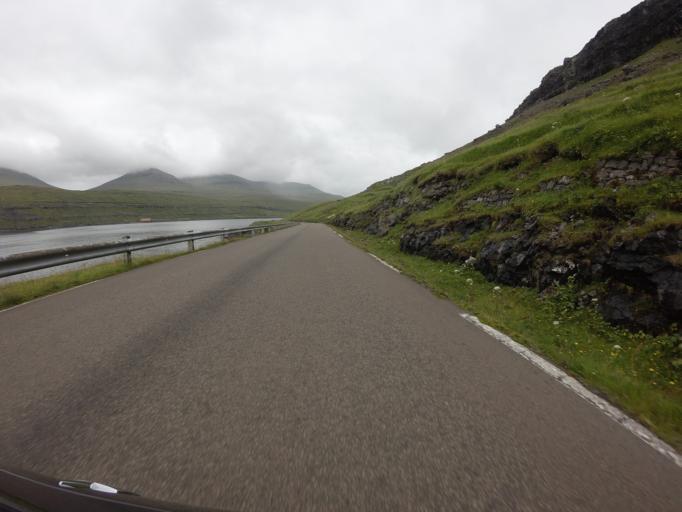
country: FO
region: Eysturoy
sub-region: Eidi
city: Eidi
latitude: 62.2825
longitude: -7.0980
